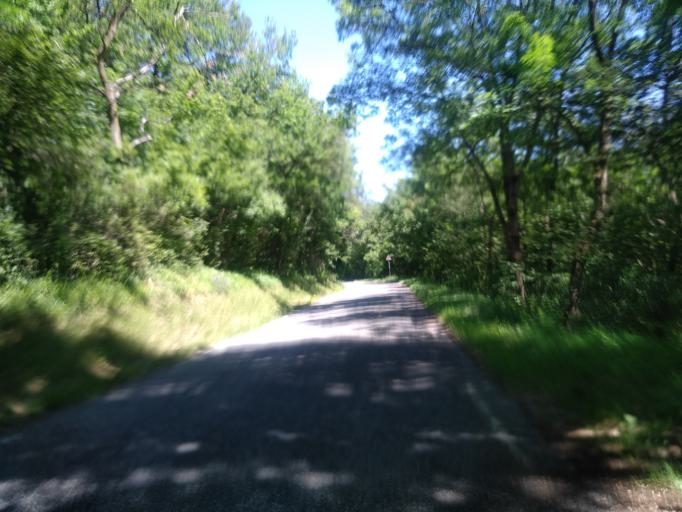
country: FR
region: Rhone-Alpes
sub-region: Departement du Rhone
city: Albigny-sur-Saone
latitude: 45.8480
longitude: 4.8091
